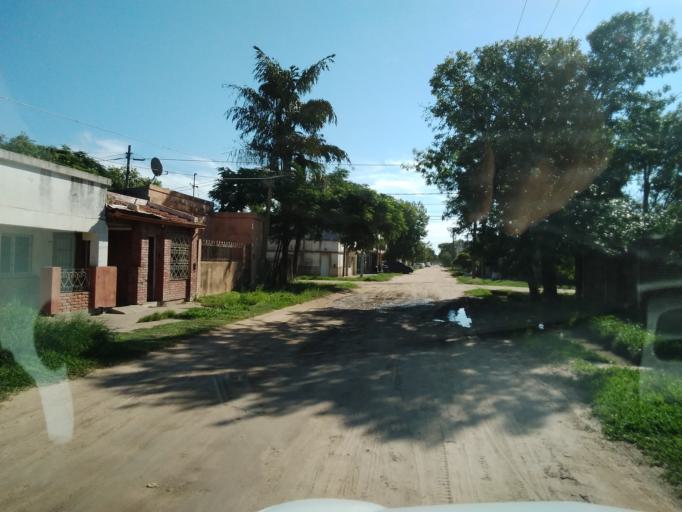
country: AR
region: Corrientes
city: Corrientes
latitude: -27.4858
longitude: -58.8046
